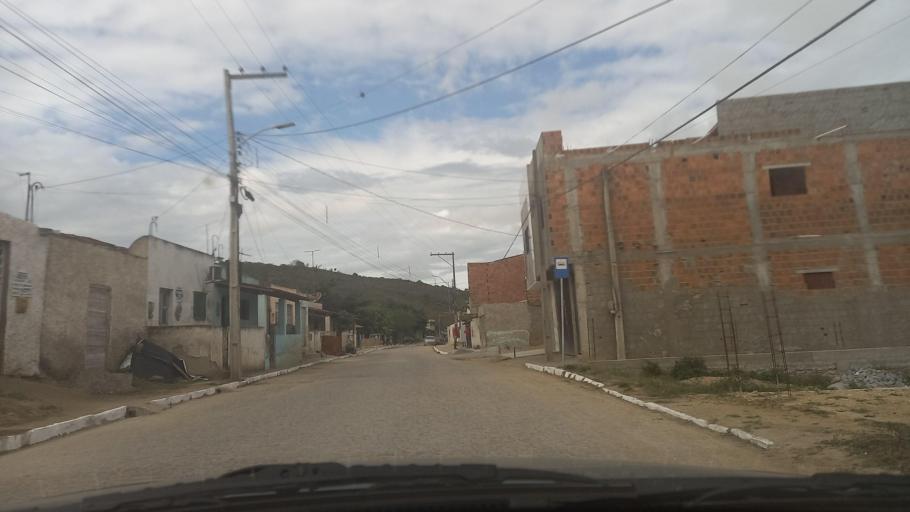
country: BR
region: Pernambuco
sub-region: Caruaru
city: Caruaru
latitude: -8.2982
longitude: -36.0305
